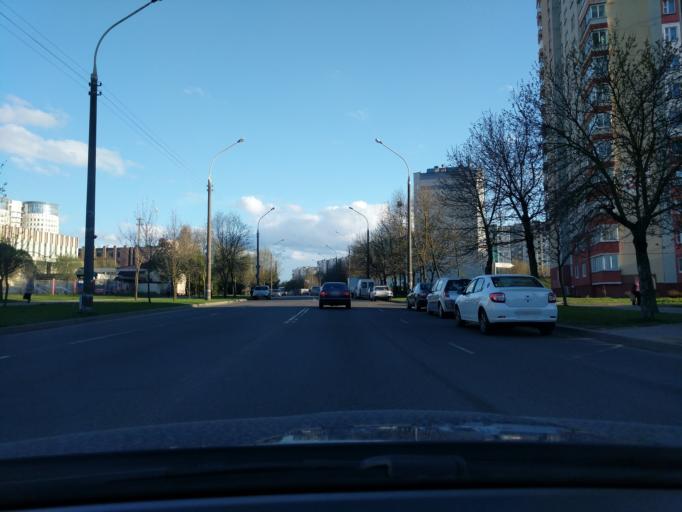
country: BY
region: Minsk
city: Novoye Medvezhino
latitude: 53.9145
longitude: 27.4499
